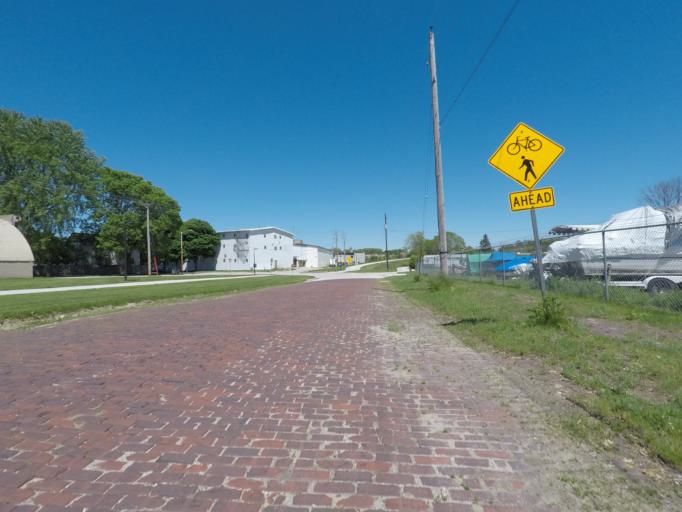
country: US
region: Wisconsin
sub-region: Sheboygan County
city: Sheboygan
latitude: 43.7526
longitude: -87.7206
